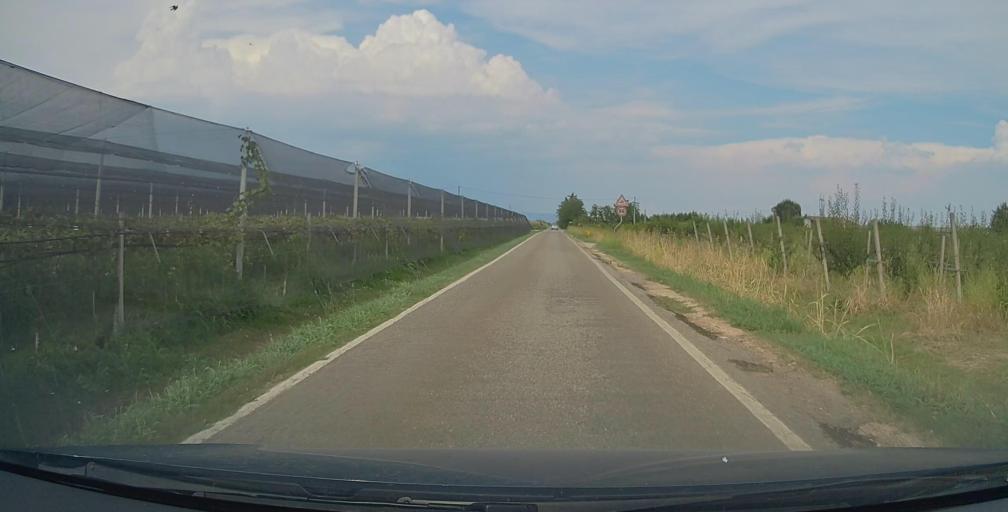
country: IT
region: Veneto
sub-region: Provincia di Verona
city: Quaderni
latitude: 45.3250
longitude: 10.7981
